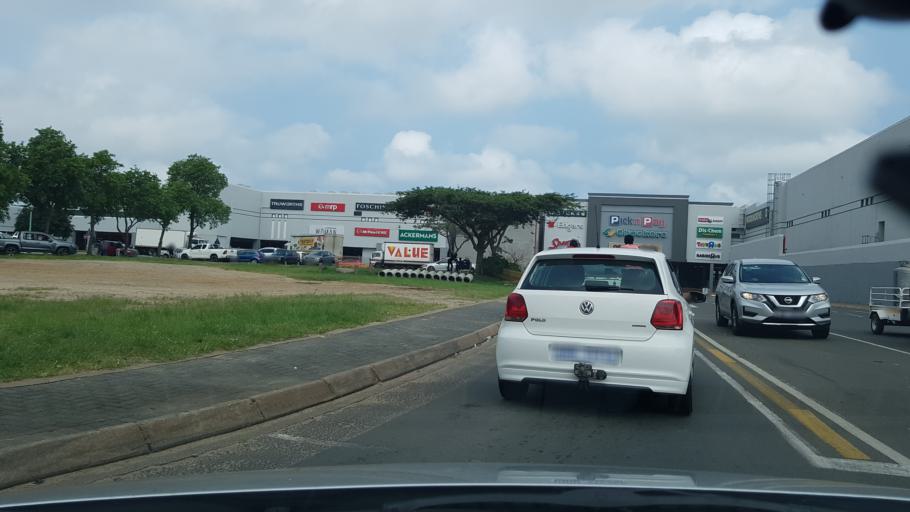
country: ZA
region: KwaZulu-Natal
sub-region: uThungulu District Municipality
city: Richards Bay
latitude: -28.7540
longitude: 32.0483
